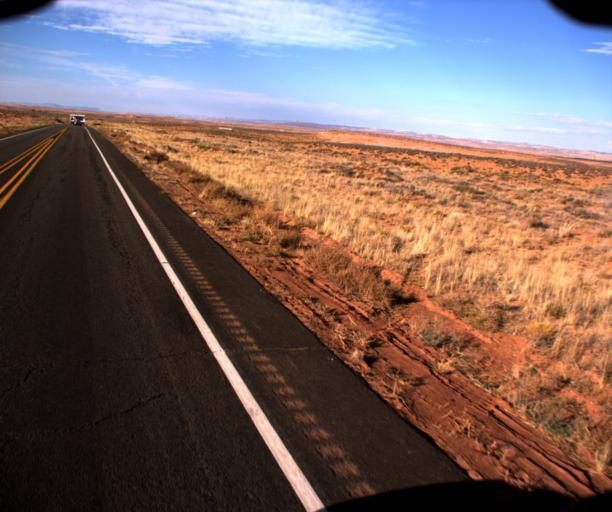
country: US
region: Arizona
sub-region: Apache County
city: Many Farms
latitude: 36.9294
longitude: -109.5775
